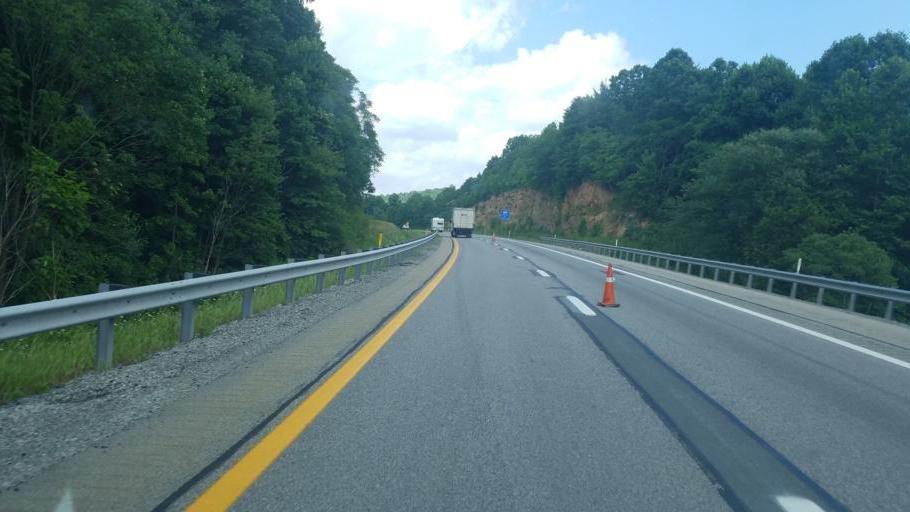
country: US
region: West Virginia
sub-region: Raleigh County
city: Bradley
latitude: 37.9275
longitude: -81.2629
